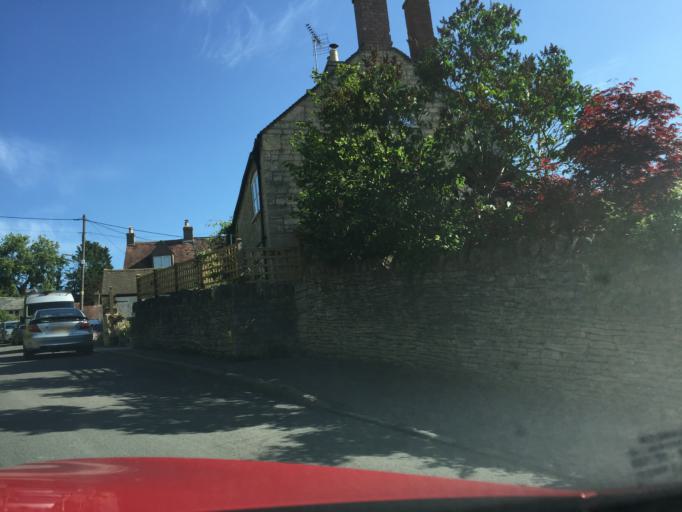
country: GB
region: England
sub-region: Gloucestershire
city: Stonehouse
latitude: 51.7537
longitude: -2.2510
